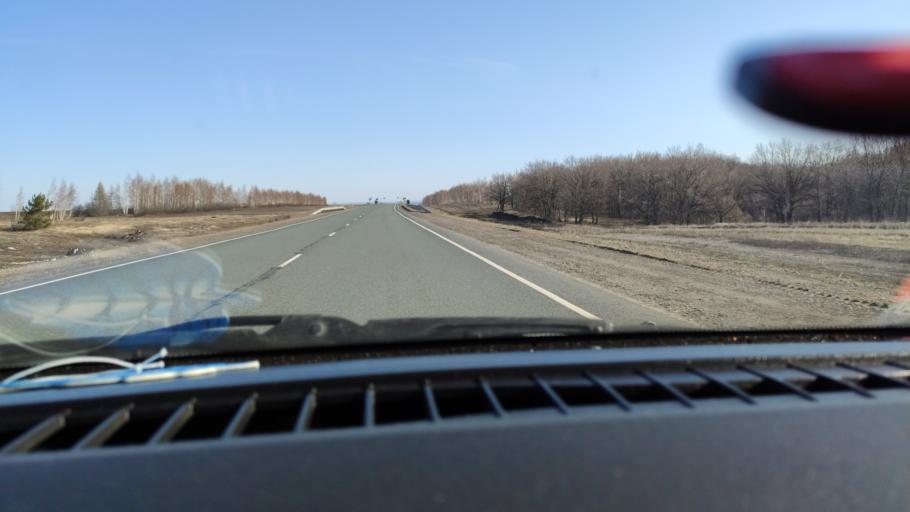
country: RU
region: Samara
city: Syzran'
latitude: 52.9481
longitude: 48.3047
